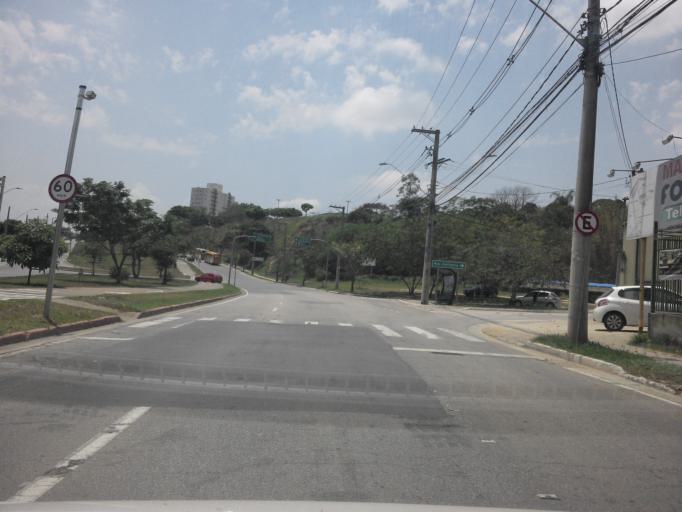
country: BR
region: Sao Paulo
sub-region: Sao Jose Dos Campos
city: Sao Jose dos Campos
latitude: -23.1686
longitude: -45.8088
